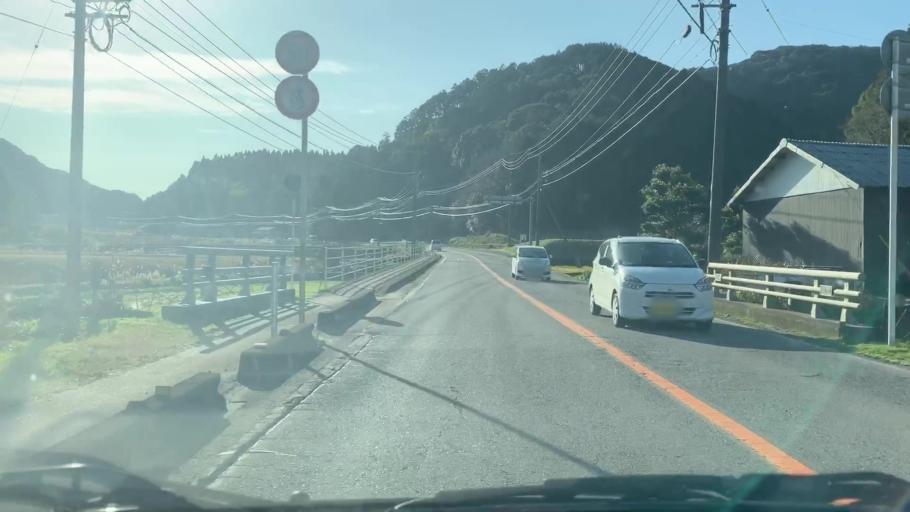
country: JP
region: Saga Prefecture
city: Takeocho-takeo
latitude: 33.2443
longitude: 130.0066
